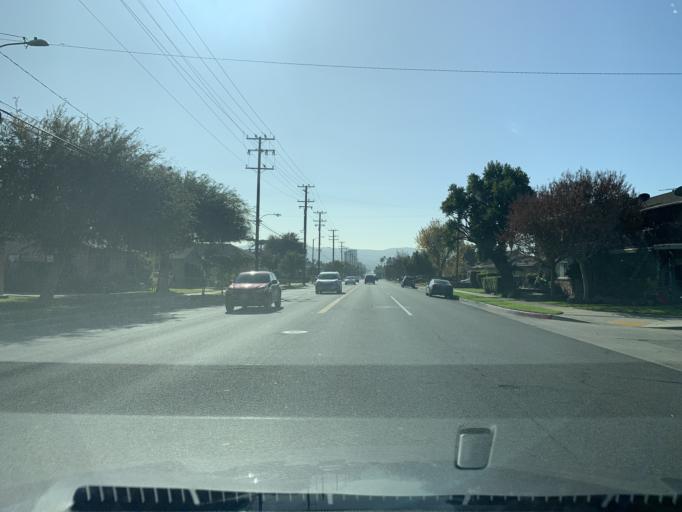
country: US
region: California
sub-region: Los Angeles County
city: Covina
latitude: 34.0850
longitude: -117.8814
